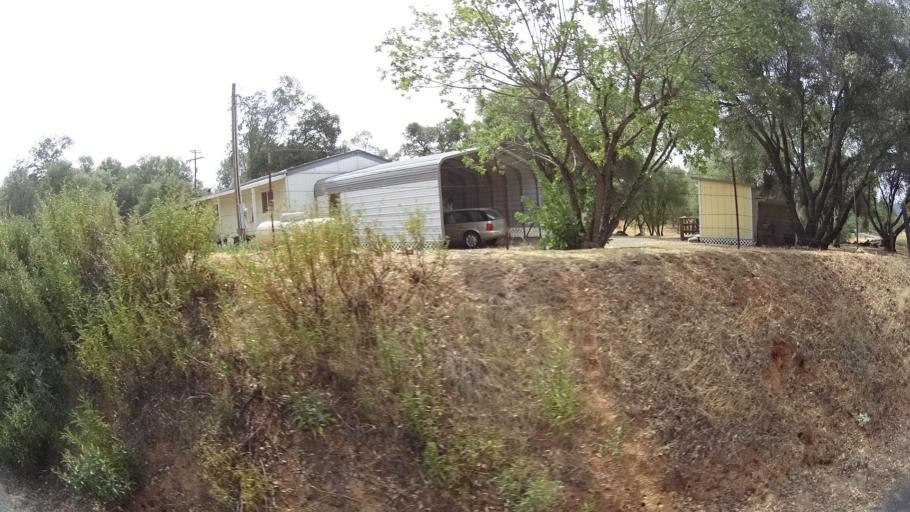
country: US
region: California
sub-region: Mariposa County
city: Midpines
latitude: 37.4802
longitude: -119.8687
